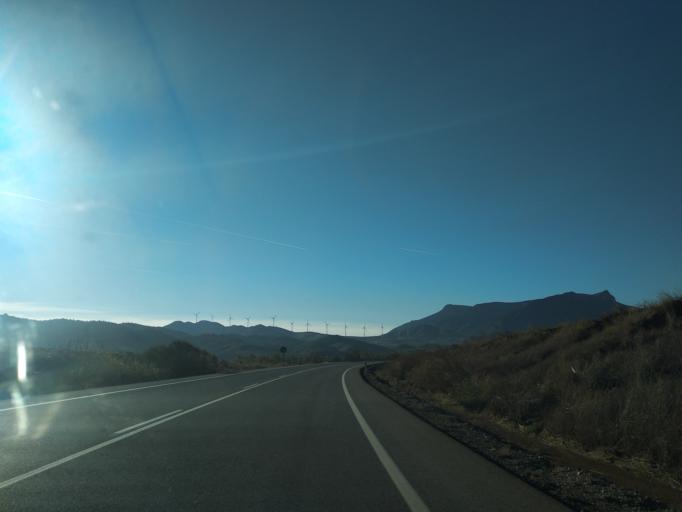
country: ES
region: Andalusia
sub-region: Provincia de Malaga
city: Ardales
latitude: 36.9044
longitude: -4.8406
